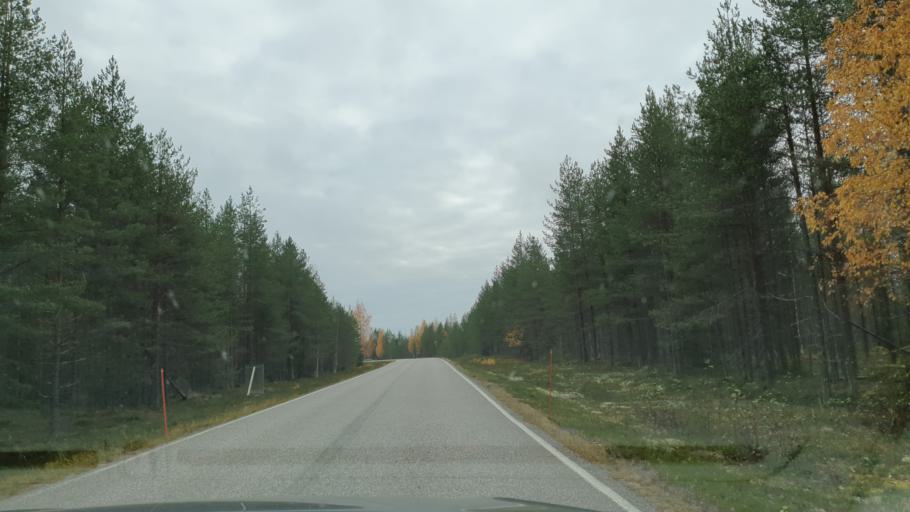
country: FI
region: Kainuu
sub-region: Kajaani
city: Paltamo
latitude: 64.6481
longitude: 27.9652
